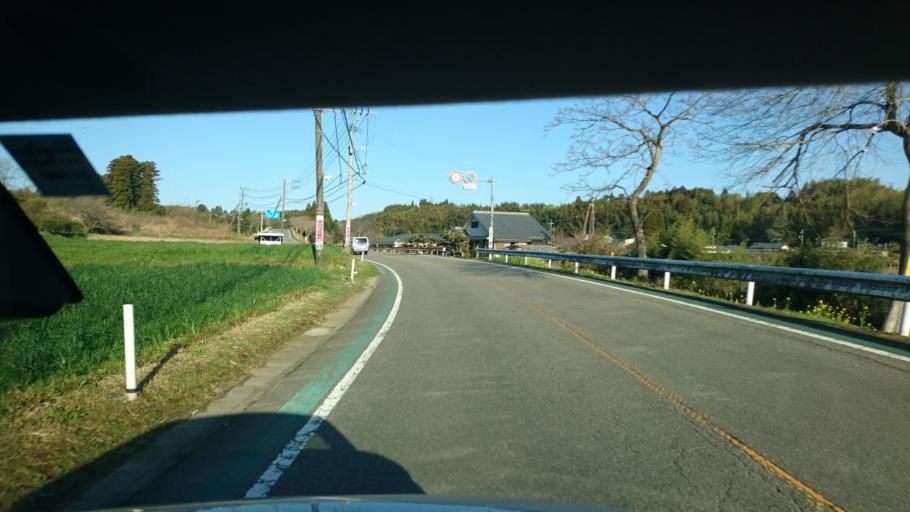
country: JP
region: Miyazaki
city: Miyazaki-shi
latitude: 31.8571
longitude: 131.3723
